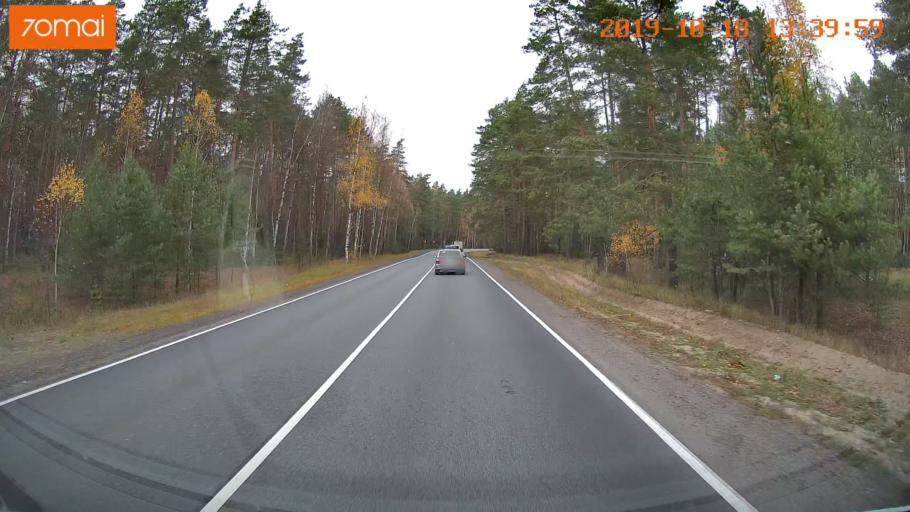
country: RU
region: Rjazan
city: Solotcha
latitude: 54.9046
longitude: 40.0026
